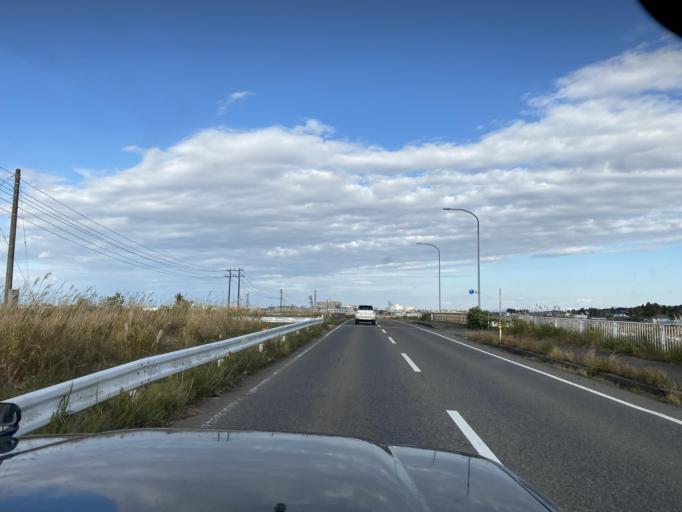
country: JP
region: Niigata
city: Niitsu-honcho
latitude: 37.7767
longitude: 139.1069
